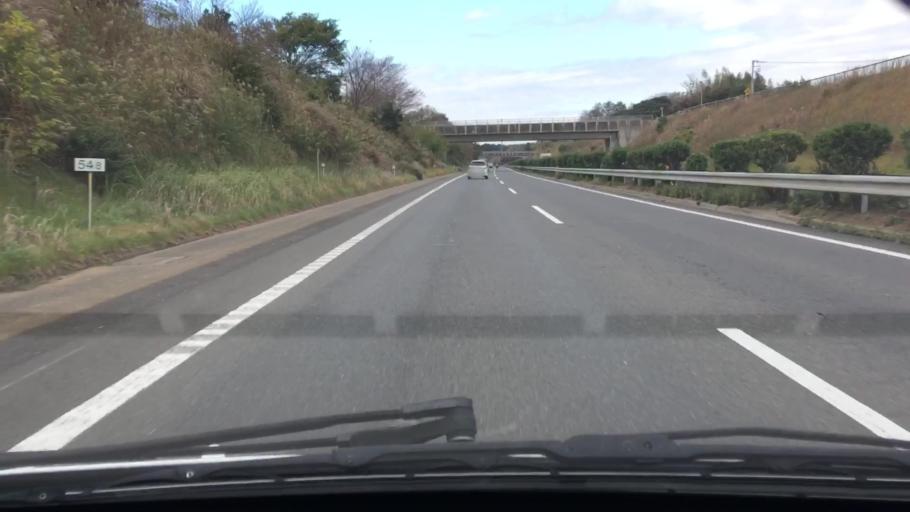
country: JP
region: Chiba
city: Ichihara
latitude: 35.4247
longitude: 140.0301
